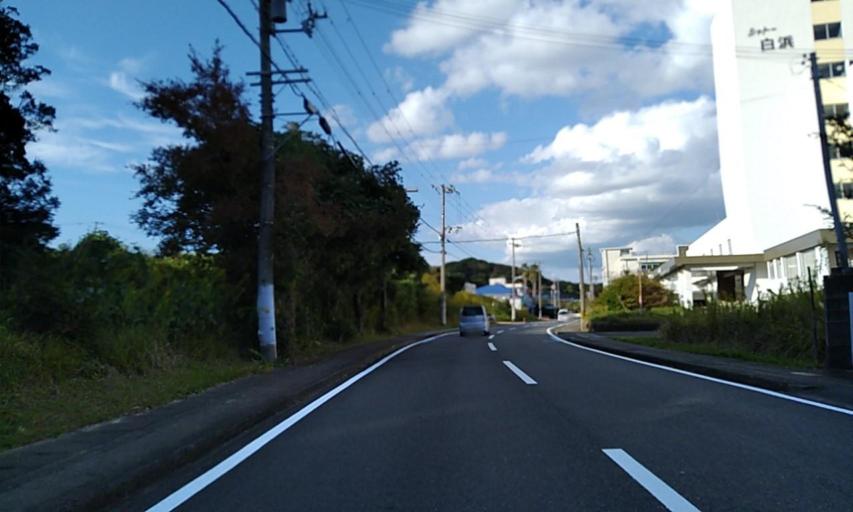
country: JP
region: Wakayama
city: Tanabe
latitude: 33.6901
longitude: 135.3555
